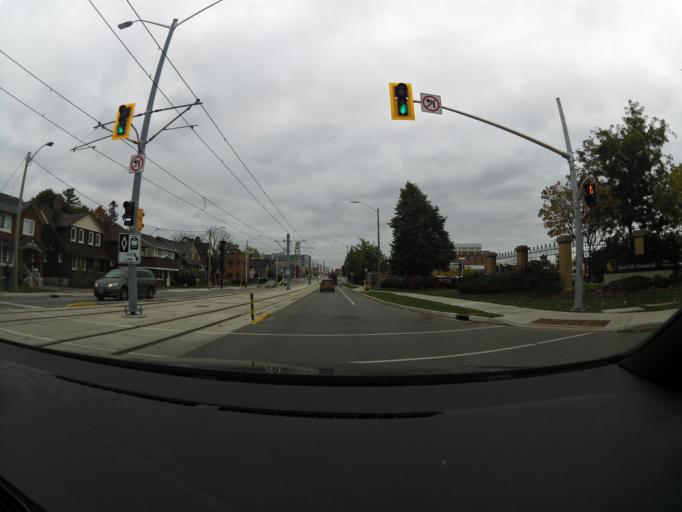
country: CA
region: Ontario
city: Waterloo
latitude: 43.4584
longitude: -80.5155
